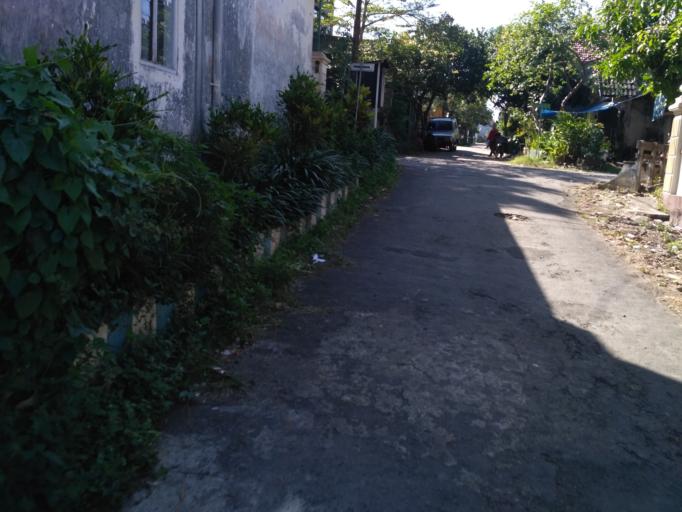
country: ID
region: East Java
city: Singosari
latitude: -7.9149
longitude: 112.6712
